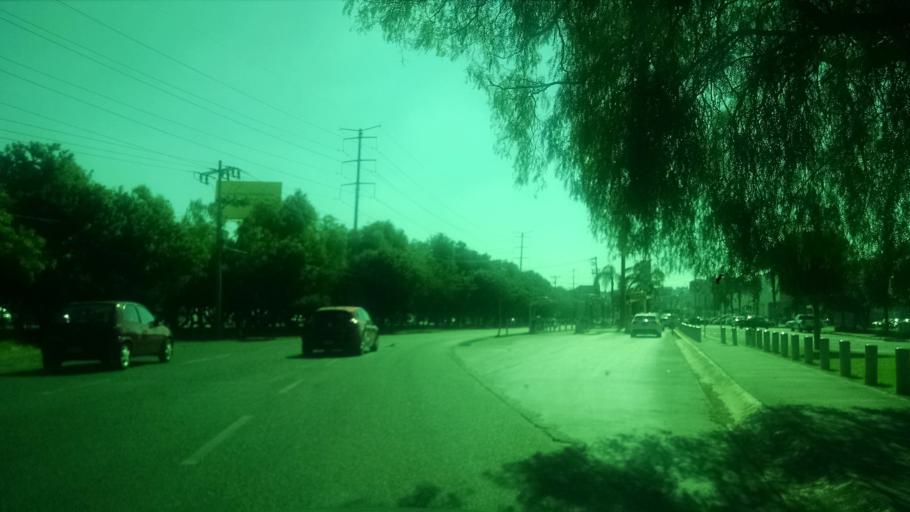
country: MX
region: Guanajuato
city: Leon
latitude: 21.1571
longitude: -101.6925
